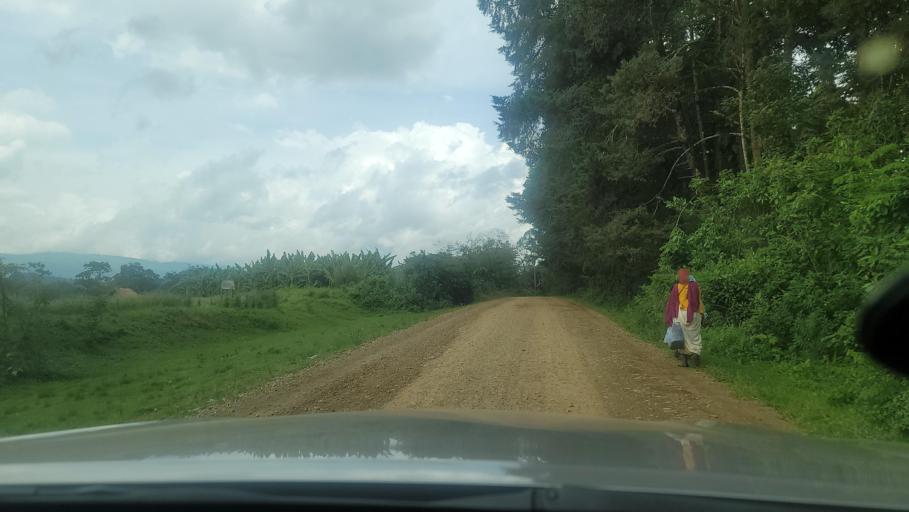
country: ET
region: Oromiya
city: Agaro
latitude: 7.7901
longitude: 36.4303
